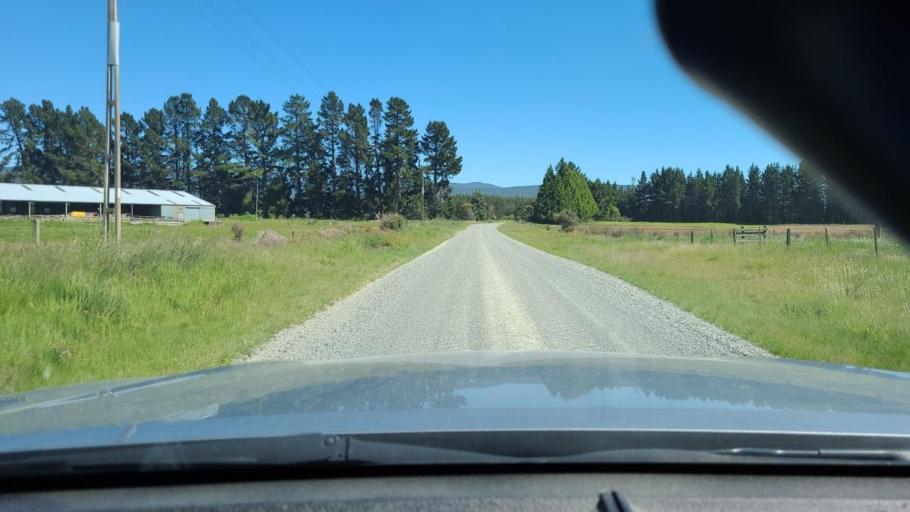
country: NZ
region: Southland
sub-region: Southland District
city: Te Anau
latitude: -45.9223
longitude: 167.6525
